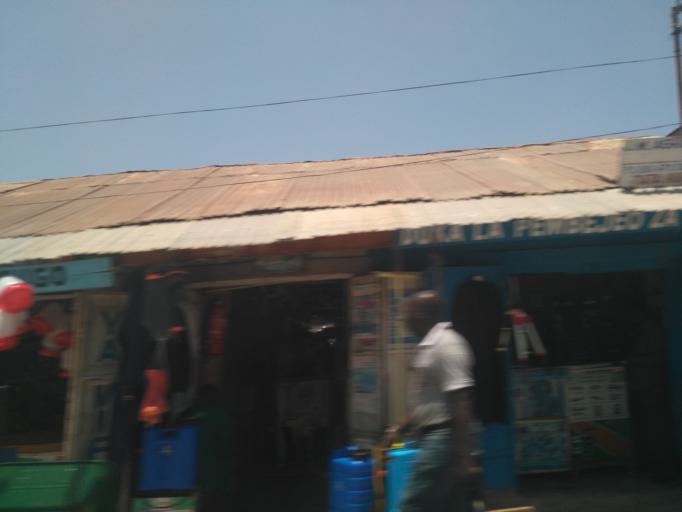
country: TZ
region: Dodoma
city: Dodoma
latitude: -6.1803
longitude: 35.7436
